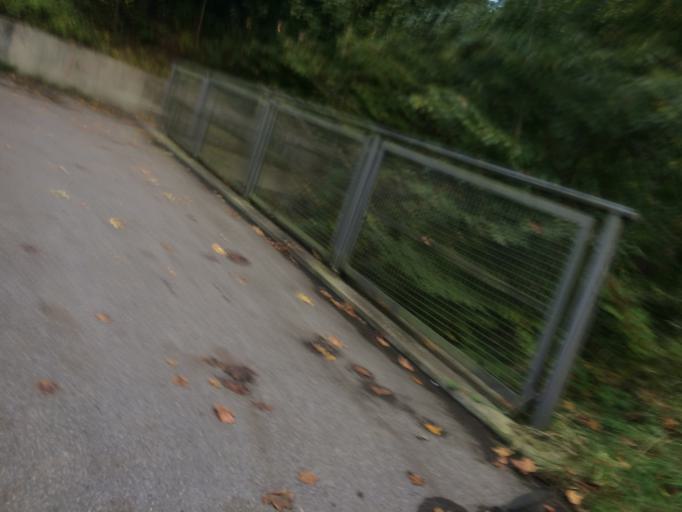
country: DE
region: Bavaria
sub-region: Swabia
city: Friedberg
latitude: 48.3517
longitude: 10.9781
